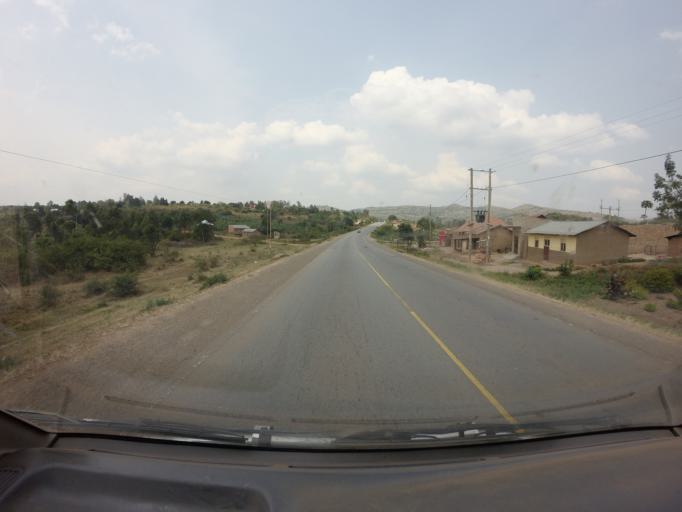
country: UG
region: Central Region
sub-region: Lyantonde District
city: Lyantonde
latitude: -0.3781
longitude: 31.2468
